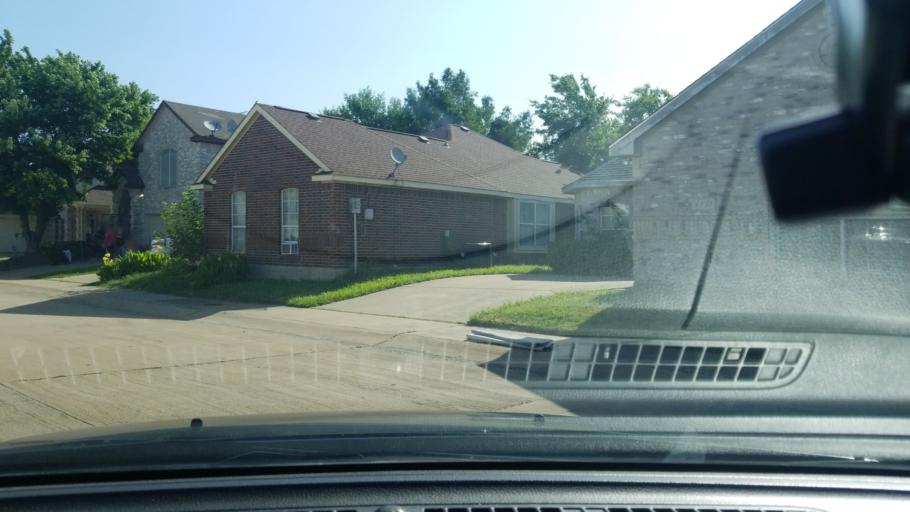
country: US
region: Texas
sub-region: Dallas County
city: Mesquite
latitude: 32.8045
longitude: -96.6781
